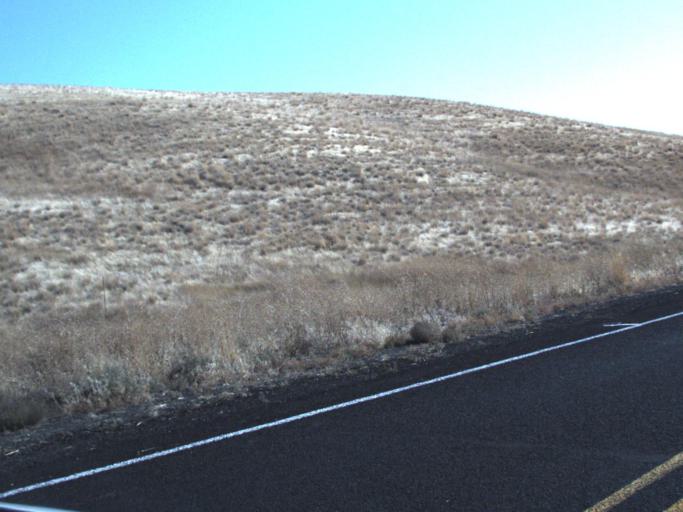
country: US
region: Washington
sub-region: Walla Walla County
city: Waitsburg
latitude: 46.2847
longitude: -118.3413
